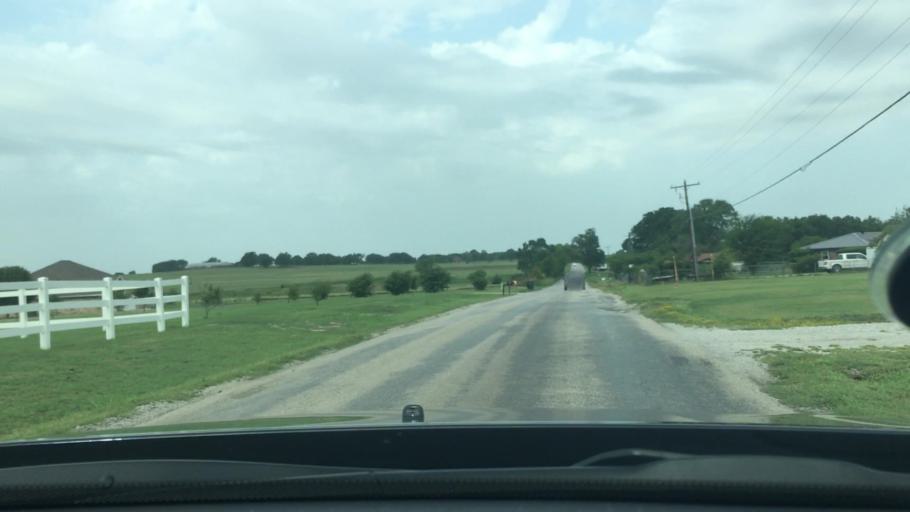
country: US
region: Oklahoma
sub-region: Carter County
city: Lone Grove
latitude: 34.2020
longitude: -97.2501
